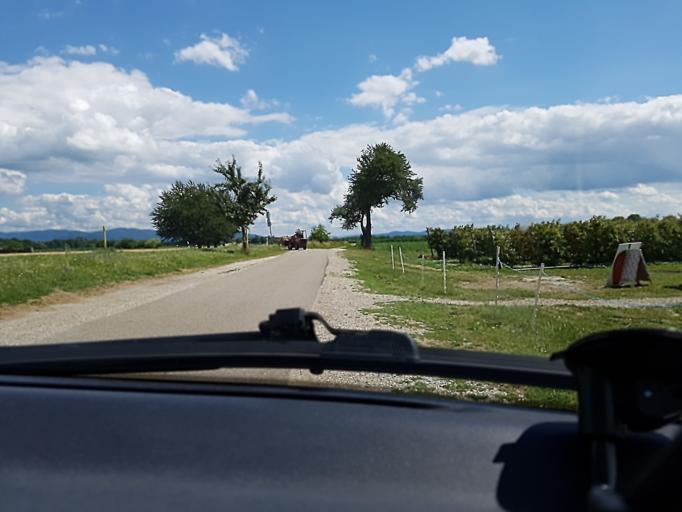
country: DE
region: Baden-Wuerttemberg
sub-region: Freiburg Region
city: Willstatt
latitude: 48.5550
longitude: 7.8787
